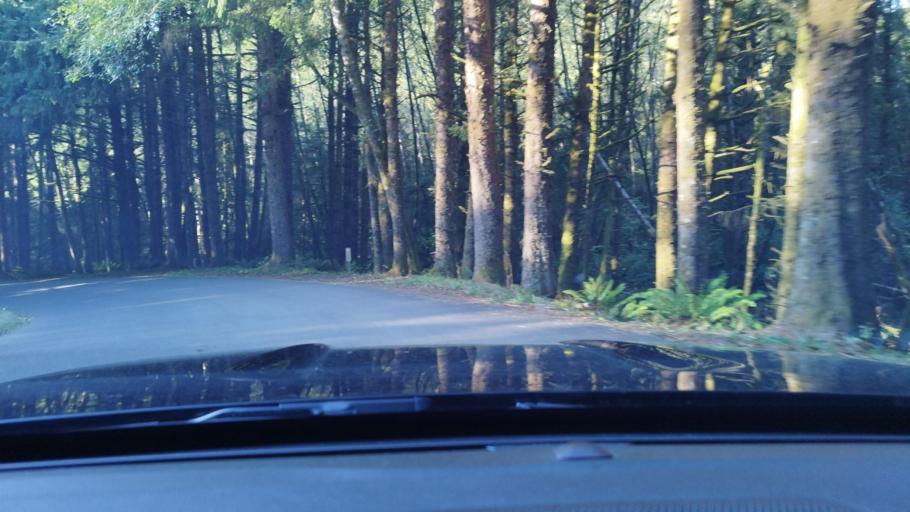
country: US
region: Oregon
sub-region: Clatsop County
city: Cannon Beach
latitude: 45.9190
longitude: -123.9707
